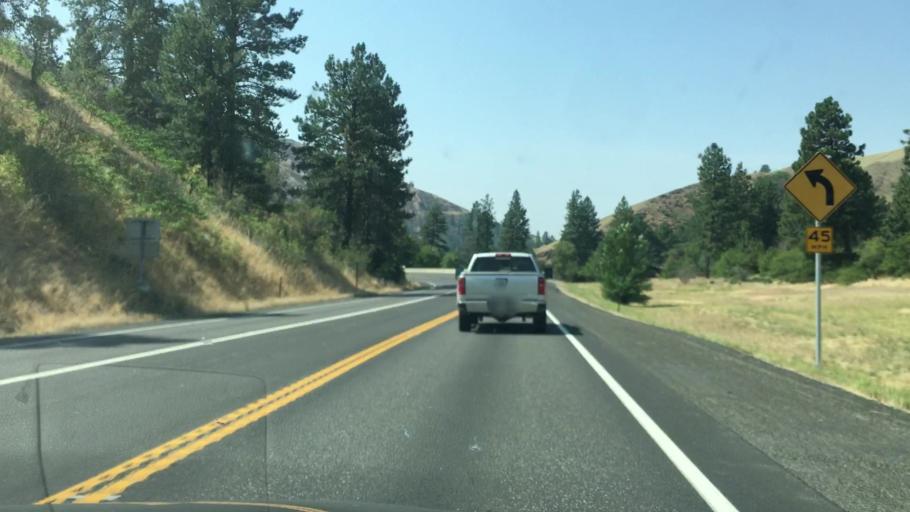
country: US
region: Idaho
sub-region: Nez Perce County
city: Lapwai
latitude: 46.4986
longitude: -116.7240
